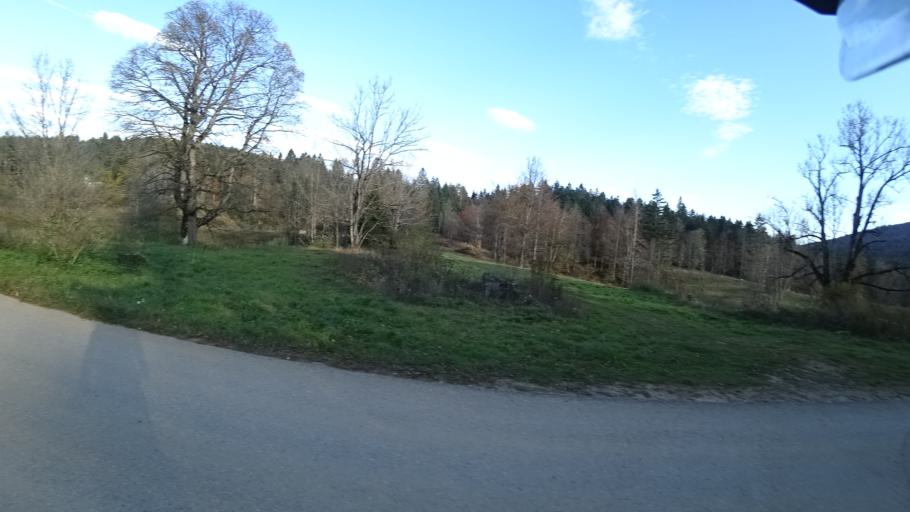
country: HR
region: Karlovacka
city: Plaski
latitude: 44.9751
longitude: 15.3986
